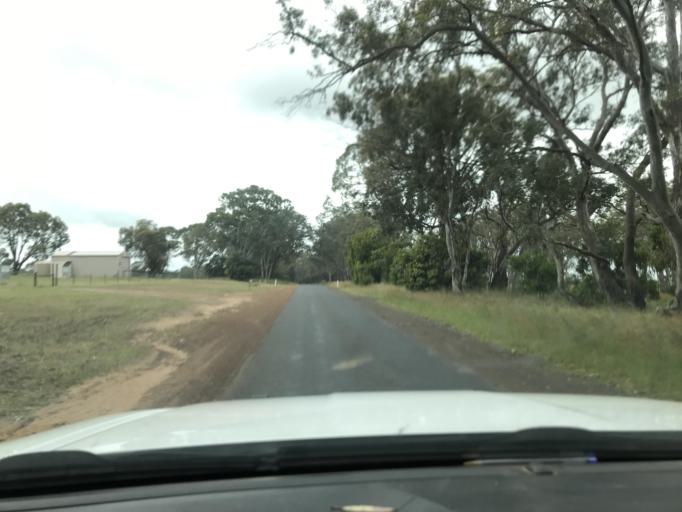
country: AU
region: South Australia
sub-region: Wattle Range
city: Penola
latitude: -37.2007
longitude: 141.4604
